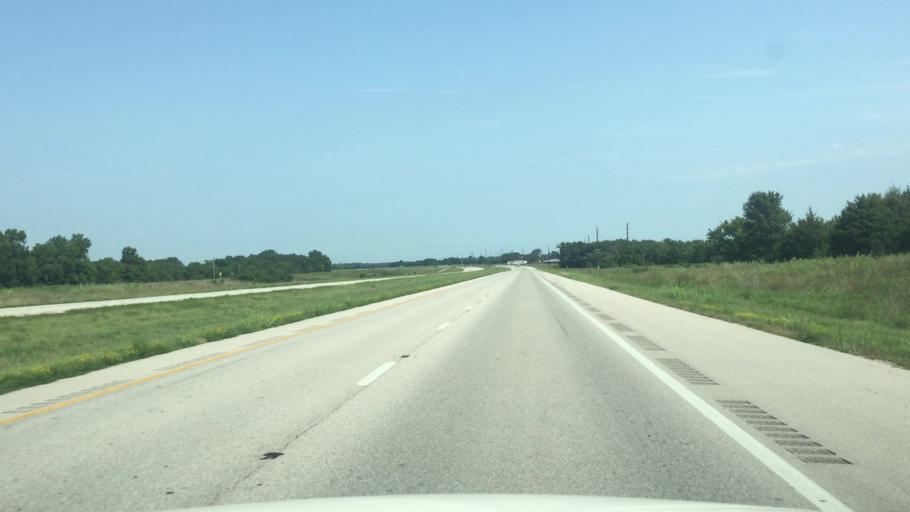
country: US
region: Kansas
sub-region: Montgomery County
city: Coffeyville
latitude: 37.0603
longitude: -95.5822
